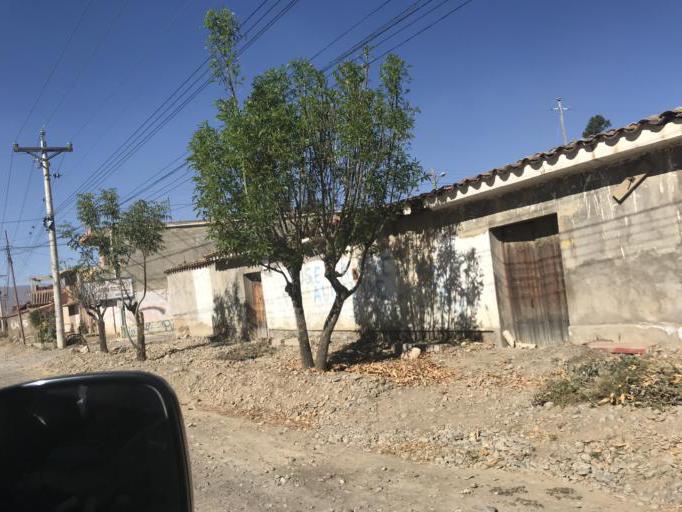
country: BO
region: Cochabamba
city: Cliza
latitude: -17.5652
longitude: -65.8875
